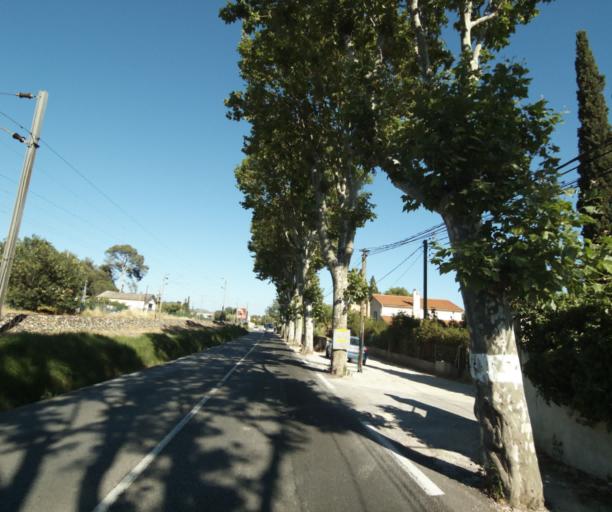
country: FR
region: Provence-Alpes-Cote d'Azur
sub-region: Departement du Var
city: La Garde
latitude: 43.1145
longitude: 5.9870
